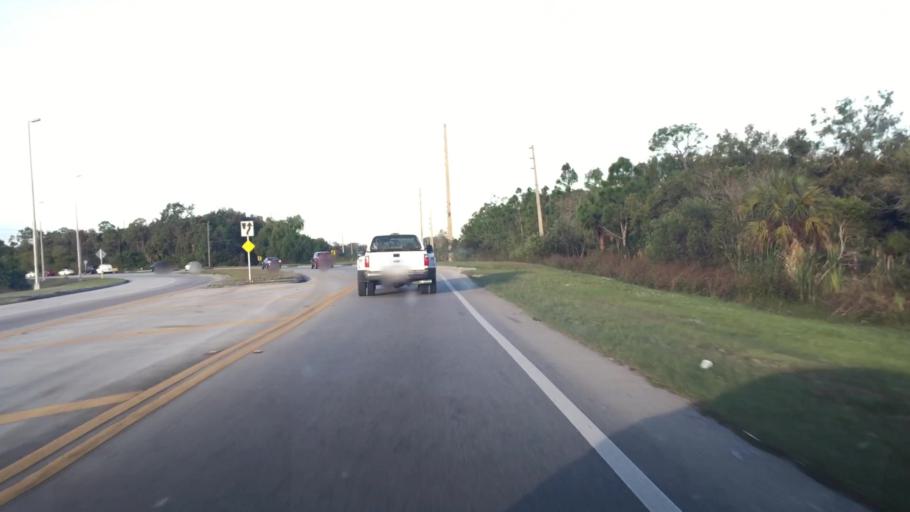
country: US
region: Florida
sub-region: Lee County
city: Gateway
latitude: 26.6275
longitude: -81.7736
